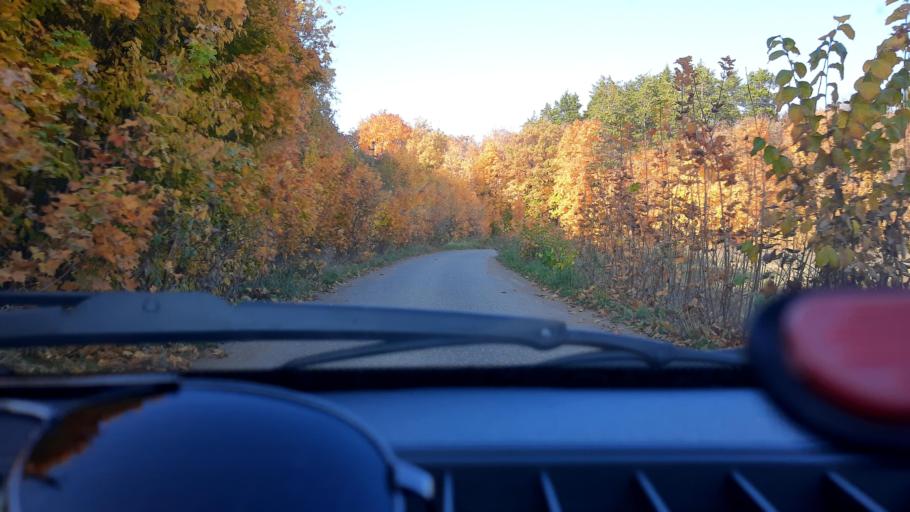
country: RU
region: Bashkortostan
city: Karmaskaly
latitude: 54.3768
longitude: 55.9104
